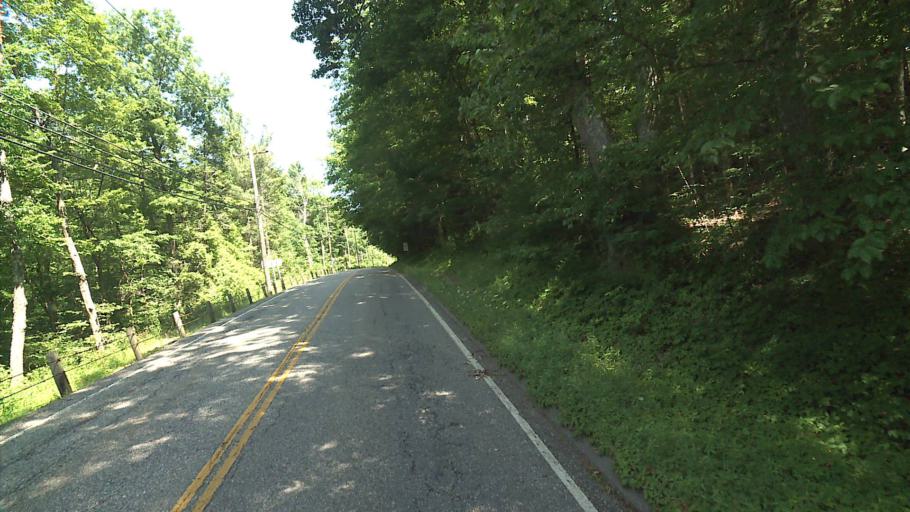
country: US
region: Connecticut
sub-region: Litchfield County
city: Canaan
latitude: 41.8621
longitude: -73.3311
